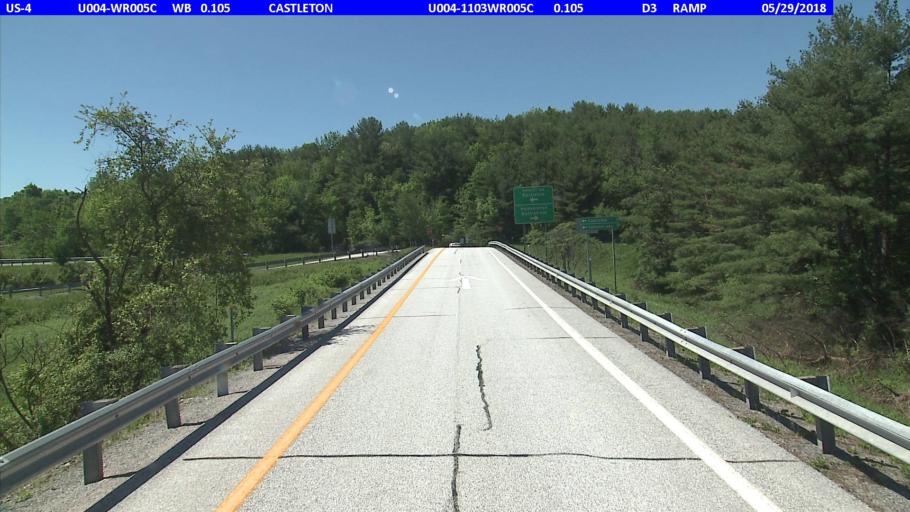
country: US
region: Vermont
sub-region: Rutland County
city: Castleton
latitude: 43.6176
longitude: -73.1628
